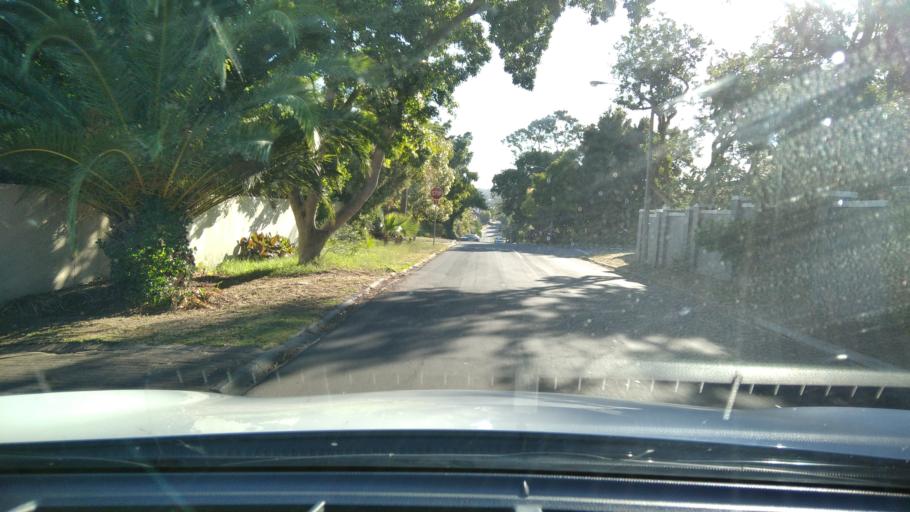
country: ZA
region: Western Cape
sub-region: City of Cape Town
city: Kraaifontein
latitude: -33.8216
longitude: 18.6585
